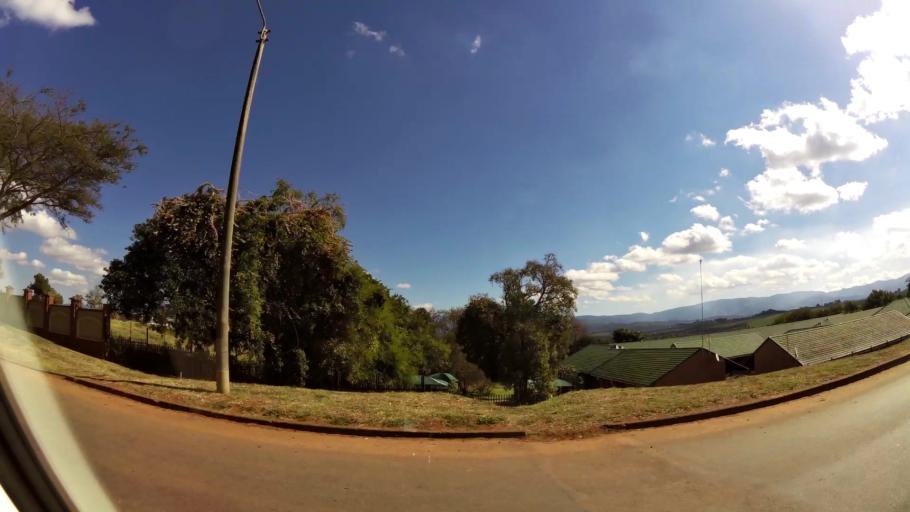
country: ZA
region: Limpopo
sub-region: Mopani District Municipality
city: Tzaneen
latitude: -23.8218
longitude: 30.1437
